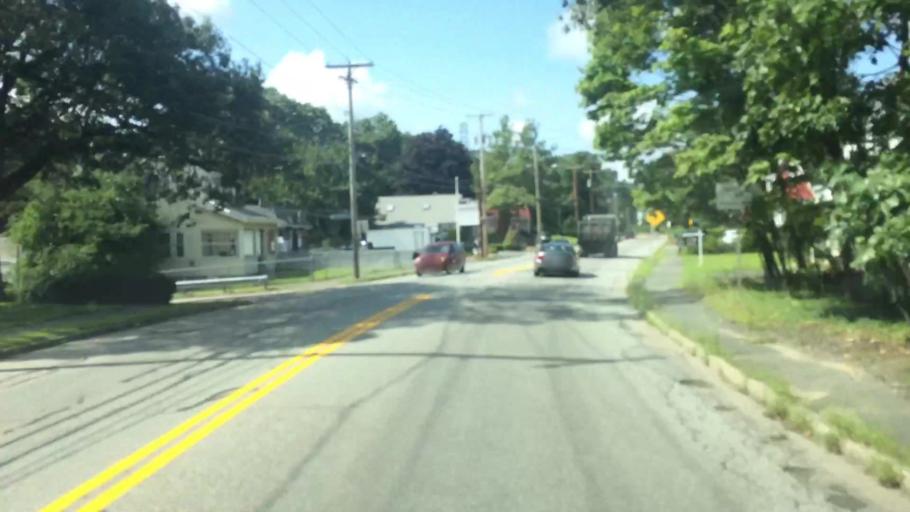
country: US
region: Massachusetts
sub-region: Essex County
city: South Peabody
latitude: 42.5026
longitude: -70.9797
